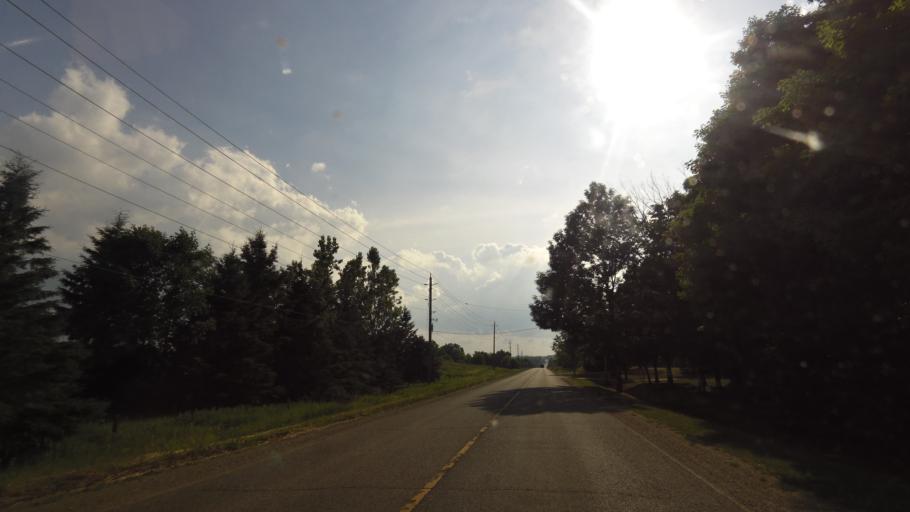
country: CA
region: Ontario
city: Orangeville
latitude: 43.9506
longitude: -80.0837
